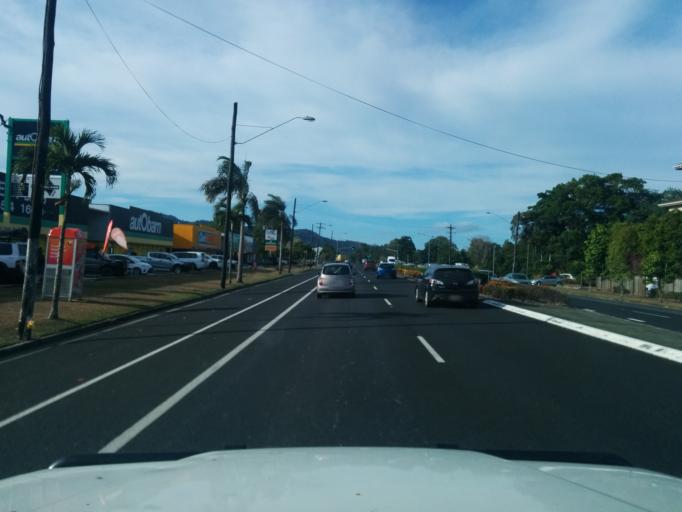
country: AU
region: Queensland
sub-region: Cairns
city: Woree
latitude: -16.9333
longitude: 145.7431
